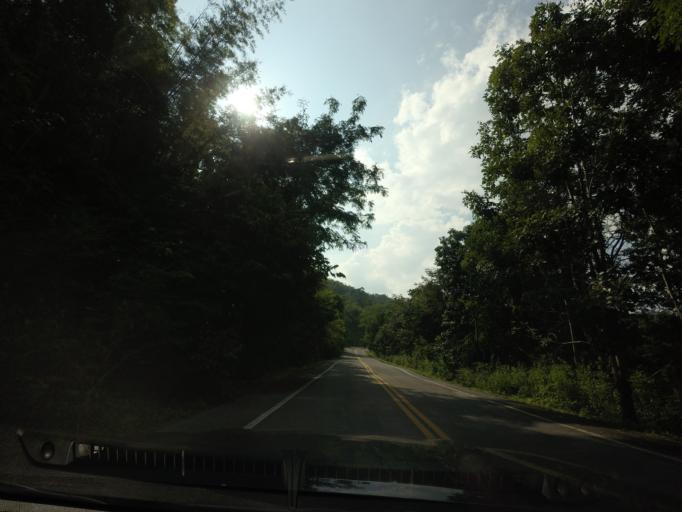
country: TH
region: Nan
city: Na Noi
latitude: 18.2739
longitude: 100.9708
